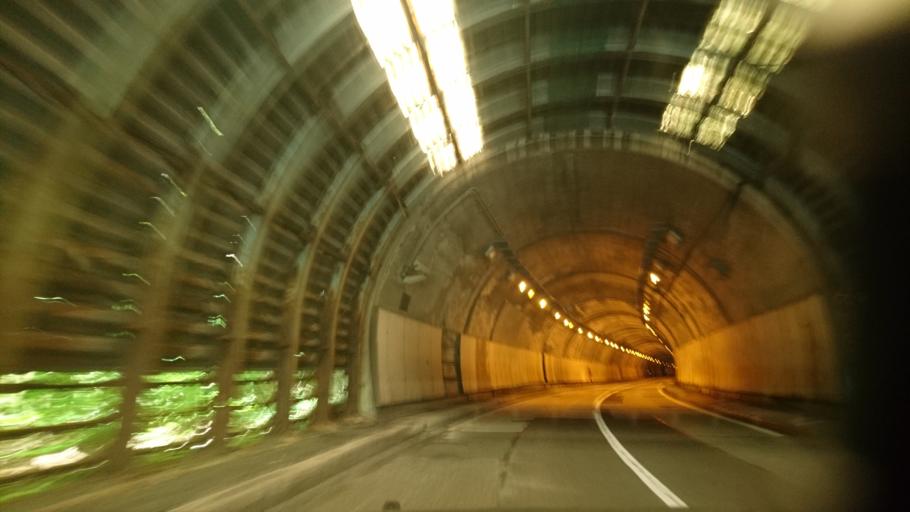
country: JP
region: Iwate
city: Shizukuishi
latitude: 39.6916
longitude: 140.7965
